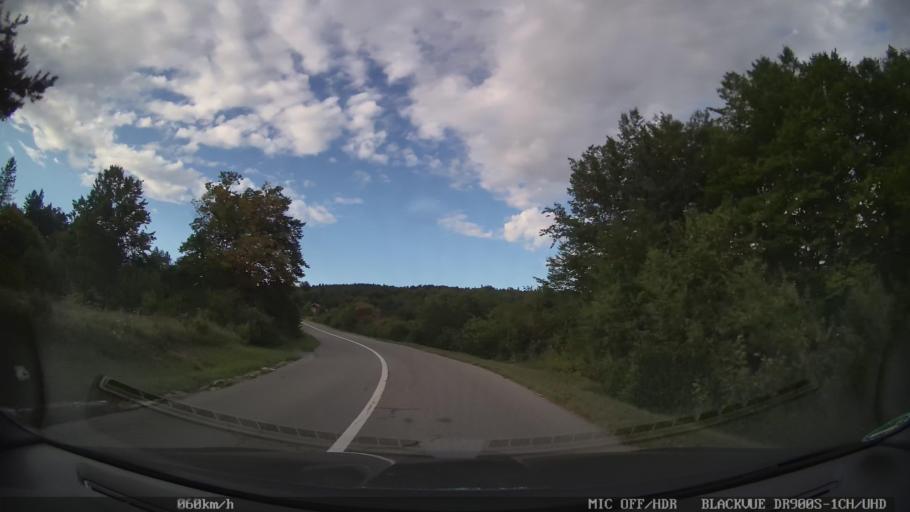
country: HR
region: Karlovacka
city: Plaski
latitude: 45.0002
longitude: 15.4276
